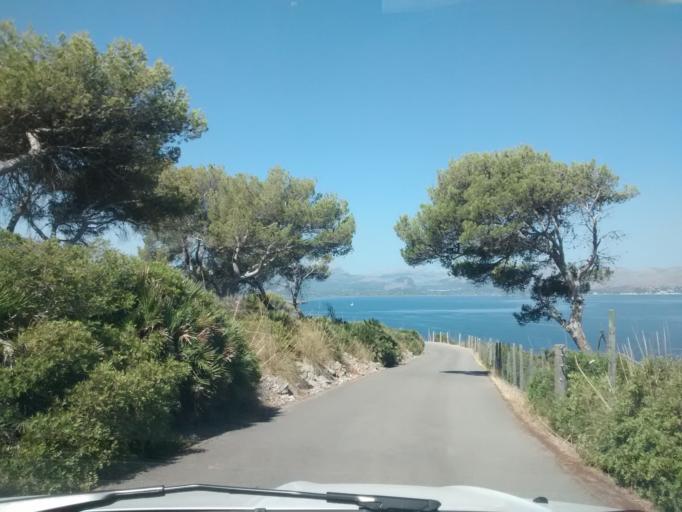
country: ES
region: Balearic Islands
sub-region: Illes Balears
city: Port d'Alcudia
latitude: 39.8745
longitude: 3.1665
